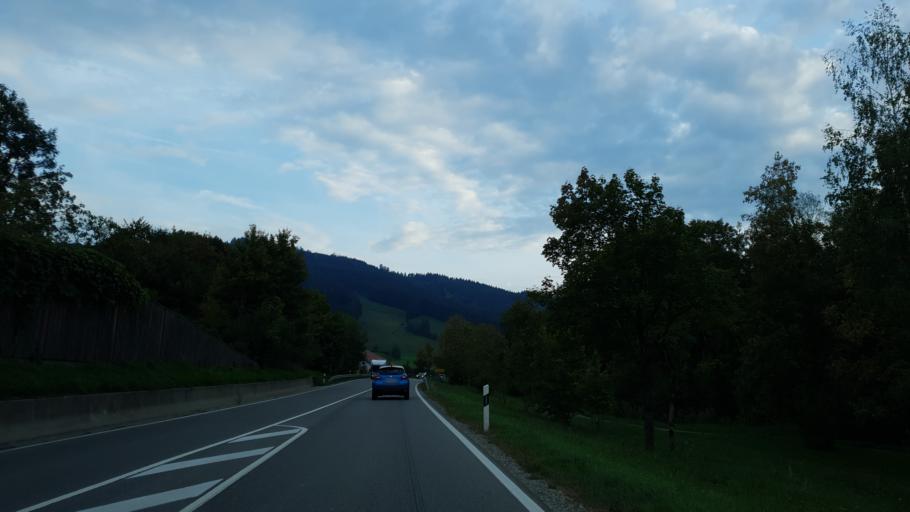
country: DE
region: Bavaria
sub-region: Swabia
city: Weitnau
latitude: 47.6650
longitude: 10.0949
